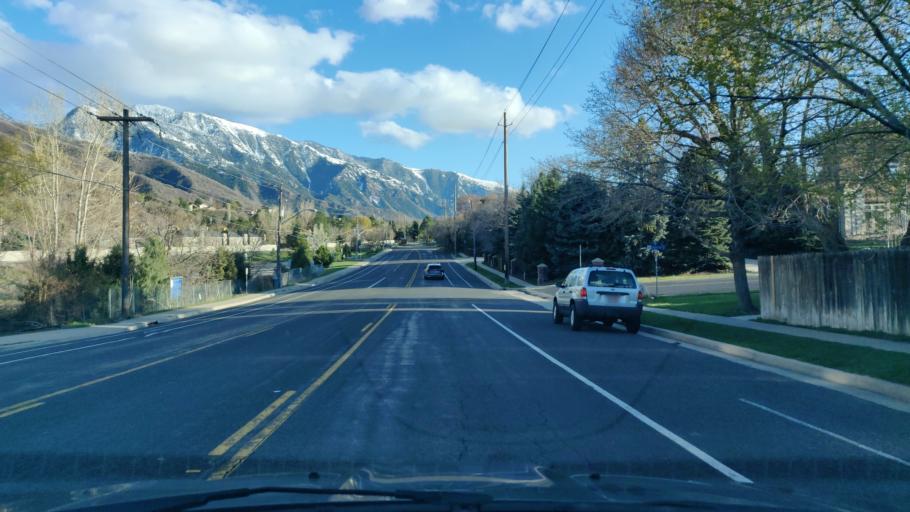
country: US
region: Utah
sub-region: Salt Lake County
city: Cottonwood Heights
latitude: 40.6053
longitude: -111.7961
